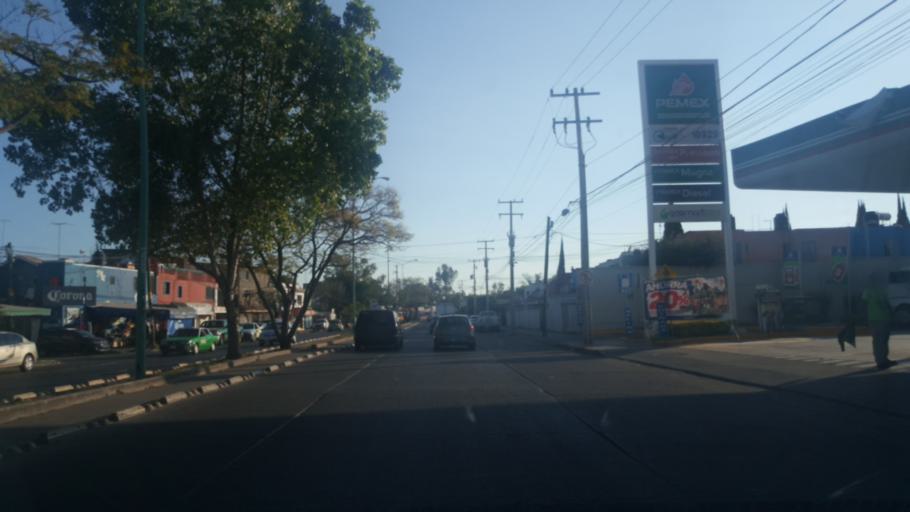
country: MX
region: Guanajuato
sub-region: Leon
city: Medina
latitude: 21.1126
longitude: -101.6348
